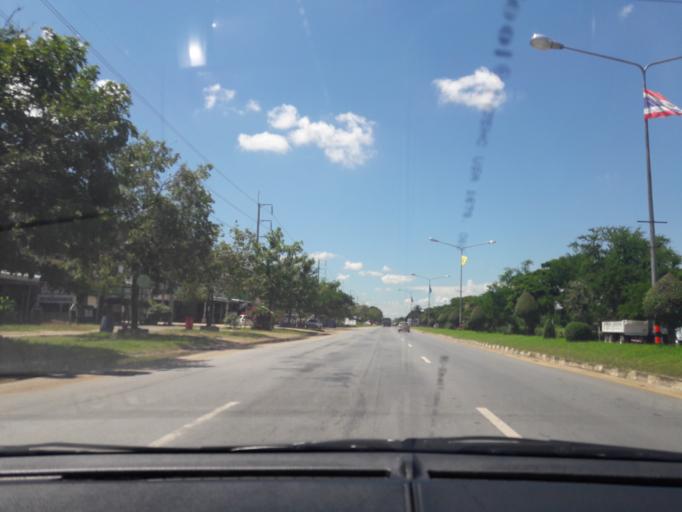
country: TH
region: Kanchanaburi
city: Tha Maka
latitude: 14.0416
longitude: 99.7876
